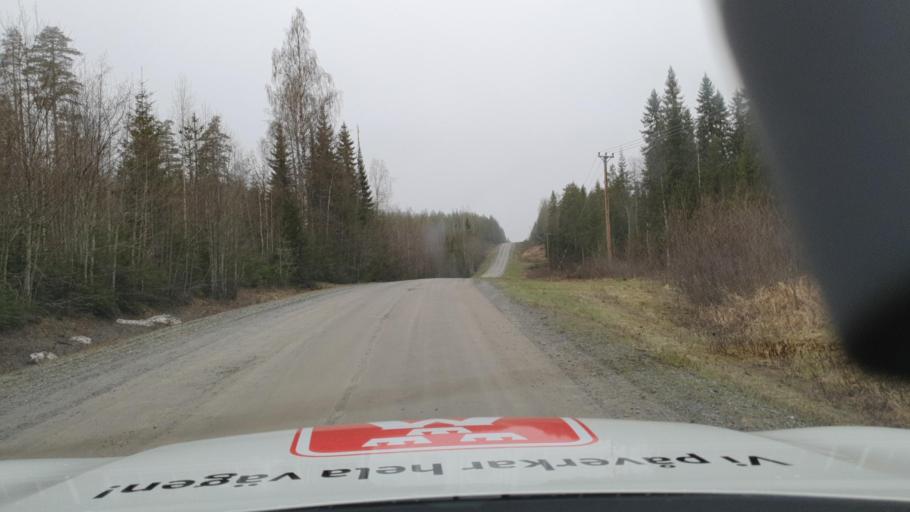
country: SE
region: Vaesterbotten
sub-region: Nordmalings Kommun
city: Nordmaling
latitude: 63.7550
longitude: 19.4940
